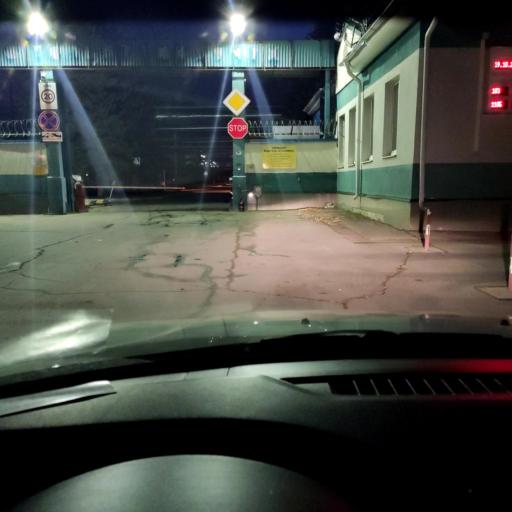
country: RU
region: Samara
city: Tol'yatti
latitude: 53.5412
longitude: 49.4448
